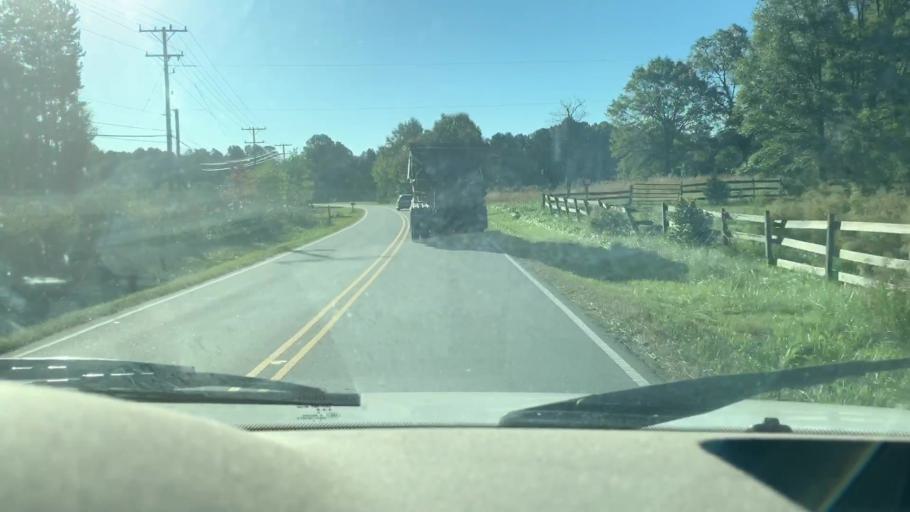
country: US
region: North Carolina
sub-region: Mecklenburg County
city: Huntersville
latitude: 35.4320
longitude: -80.7623
